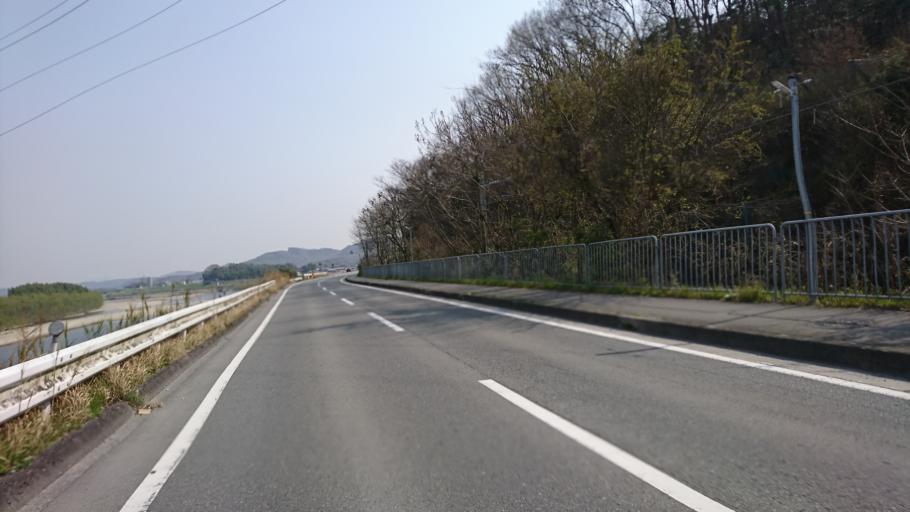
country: JP
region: Hyogo
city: Ono
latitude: 34.8454
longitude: 134.9106
